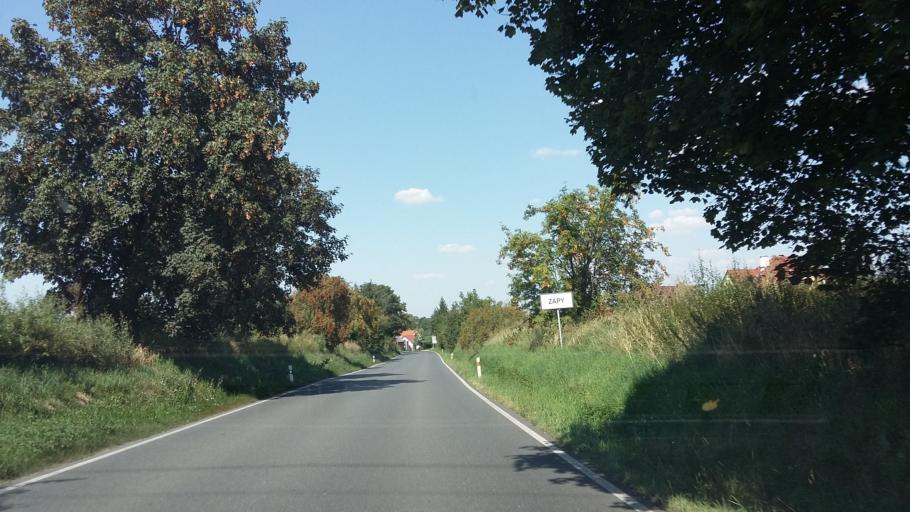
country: CZ
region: Central Bohemia
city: Brandys nad Labem-Stara Boleslav
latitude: 50.1601
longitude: 14.6813
